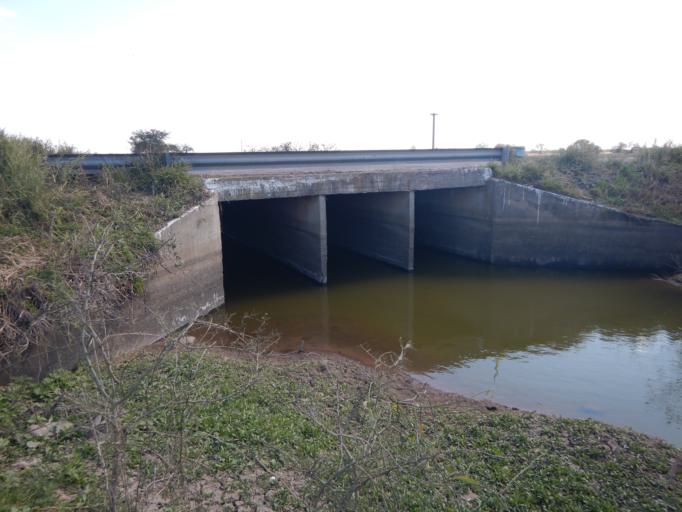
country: AR
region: Santa Fe
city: Tostado
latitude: -28.6749
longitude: -61.5312
